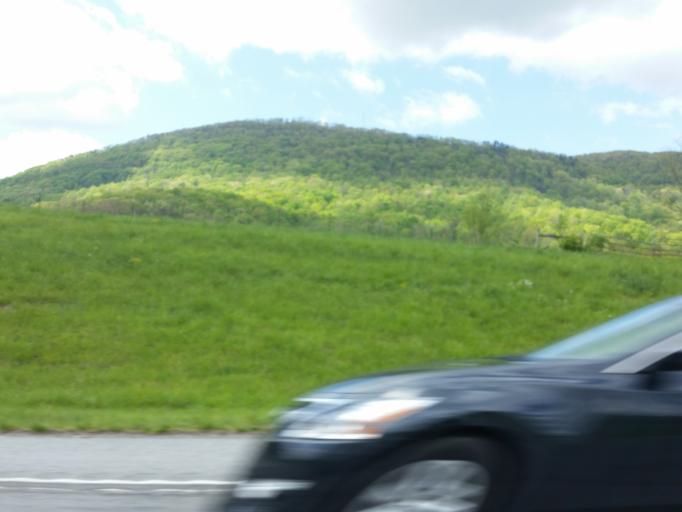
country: US
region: Tennessee
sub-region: Campbell County
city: Fincastle
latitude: 36.4633
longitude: -83.8659
